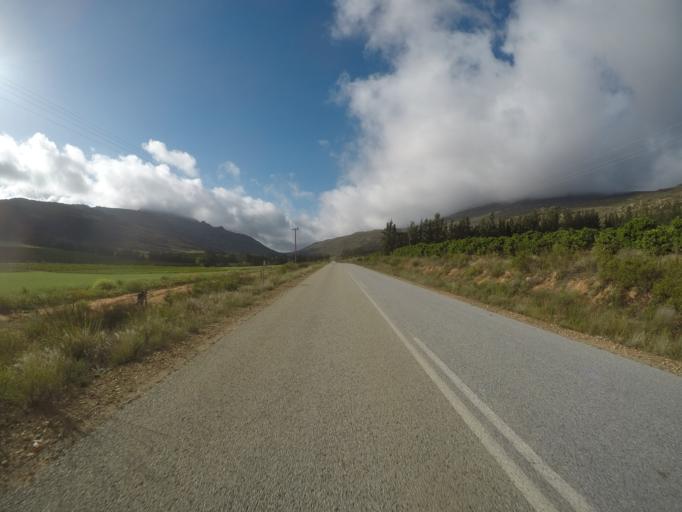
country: ZA
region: Western Cape
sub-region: West Coast District Municipality
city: Clanwilliam
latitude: -32.3554
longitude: 18.8509
